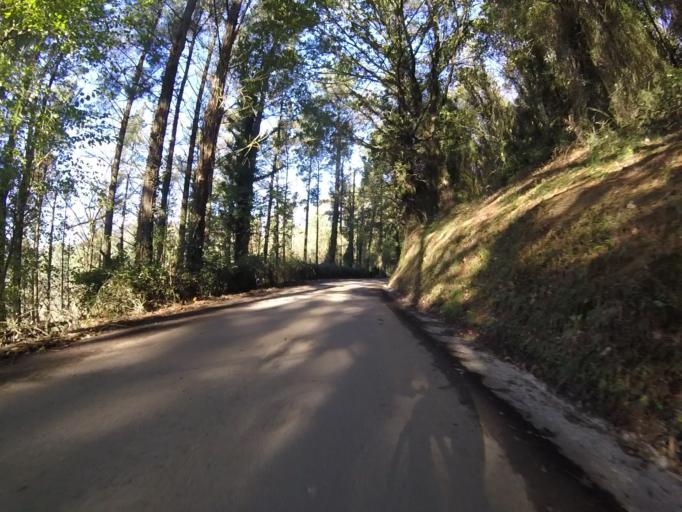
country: ES
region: Basque Country
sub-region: Provincia de Guipuzcoa
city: Usurbil
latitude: 43.2862
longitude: -2.0705
